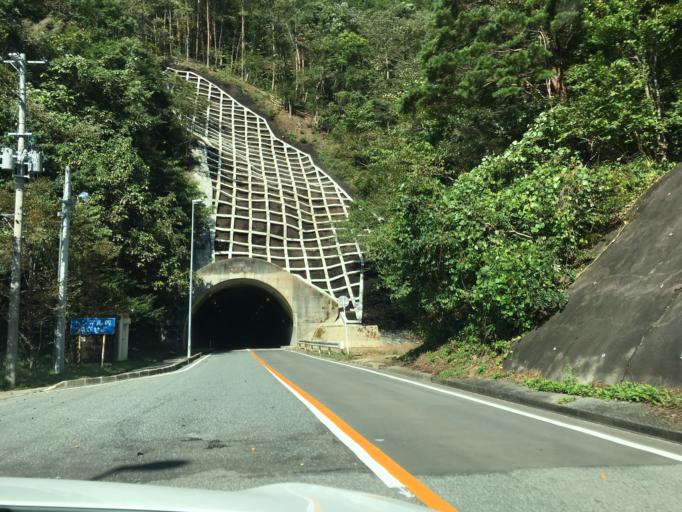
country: JP
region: Fukushima
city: Namie
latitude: 37.5146
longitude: 140.8914
